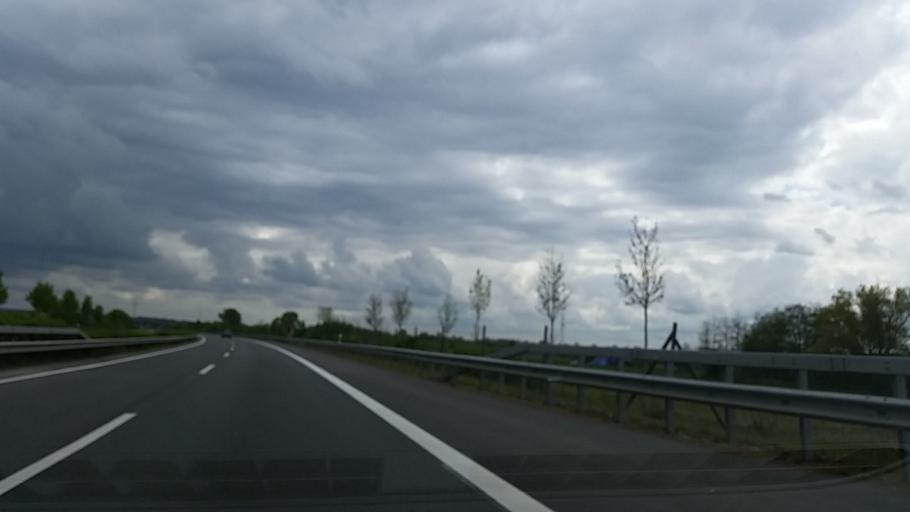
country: DE
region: Lower Saxony
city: Horneburg
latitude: 53.5293
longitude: 9.5795
